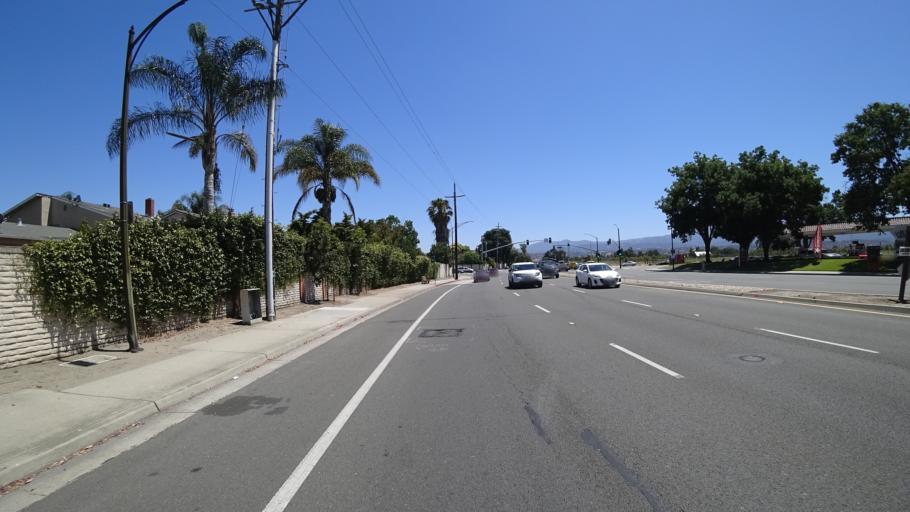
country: US
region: California
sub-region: Santa Clara County
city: Seven Trees
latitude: 37.2668
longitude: -121.8311
